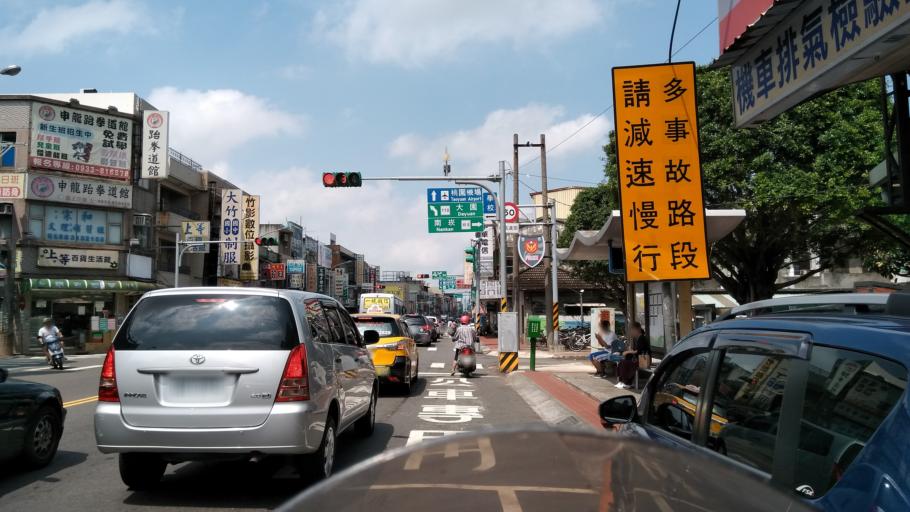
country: TW
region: Taiwan
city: Taoyuan City
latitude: 25.0241
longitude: 121.2593
